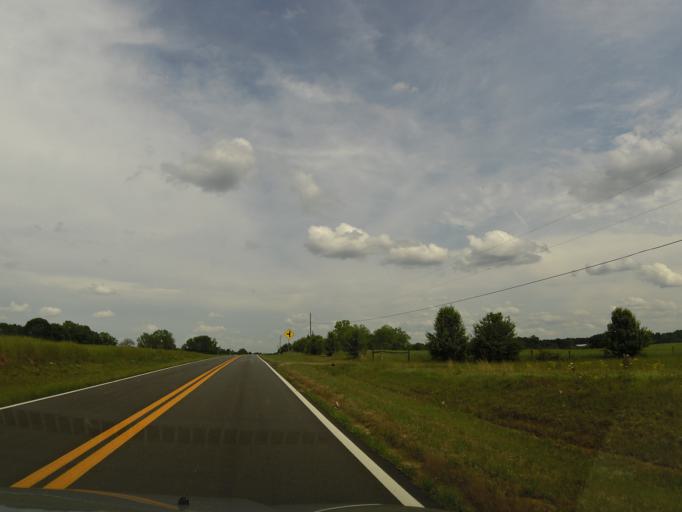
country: US
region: Georgia
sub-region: McDuffie County
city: Thomson
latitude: 33.5284
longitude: -82.4779
